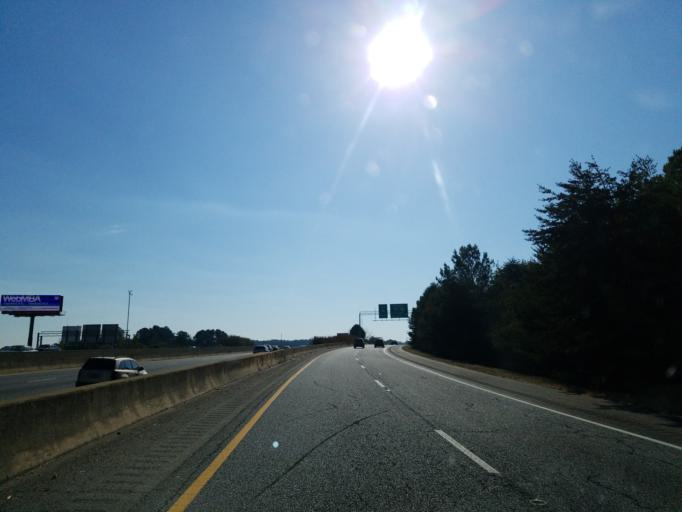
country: US
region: Georgia
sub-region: Fulton County
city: College Park
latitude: 33.6263
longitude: -84.4567
